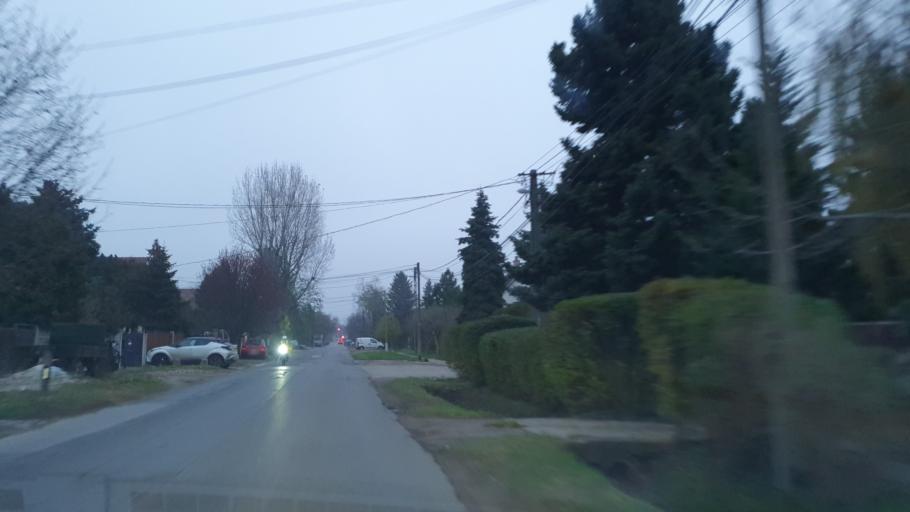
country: HU
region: Pest
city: Csomor
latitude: 47.5292
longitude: 19.2247
